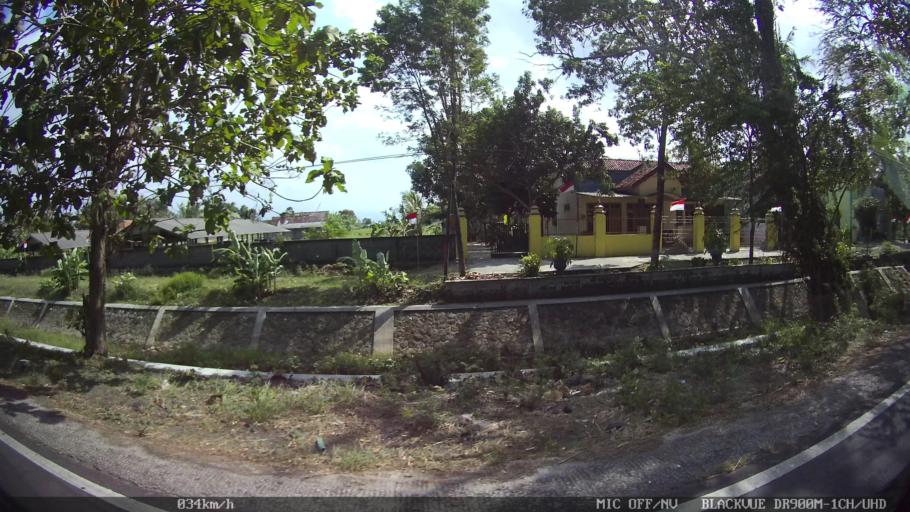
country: ID
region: Daerah Istimewa Yogyakarta
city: Srandakan
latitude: -7.8956
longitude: 110.1541
